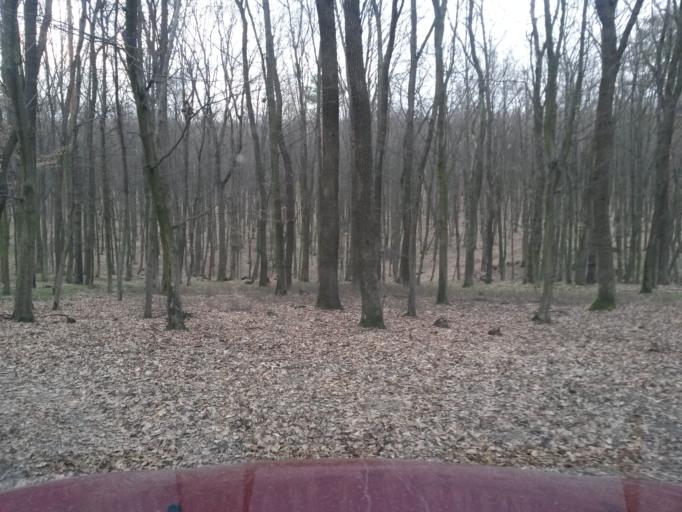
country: SK
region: Kosicky
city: Kosice
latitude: 48.6974
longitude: 21.3025
